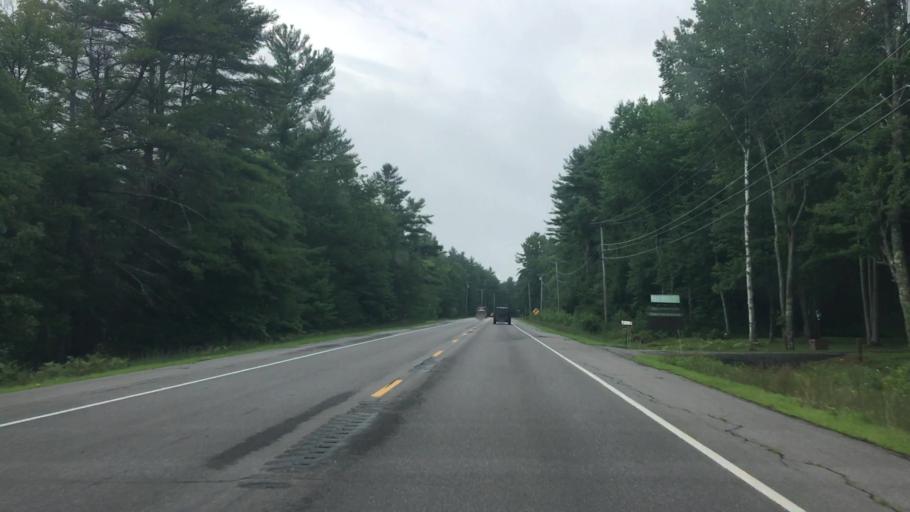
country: US
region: Maine
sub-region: York County
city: Lebanon
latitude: 43.3861
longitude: -70.8765
